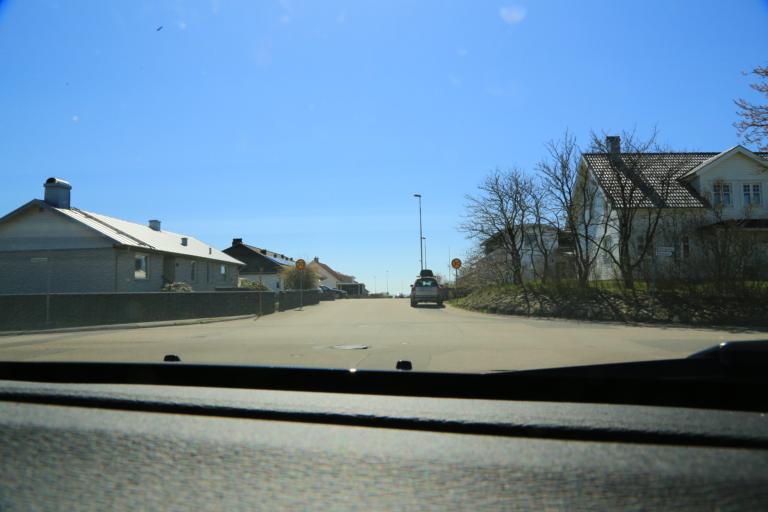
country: SE
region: Halland
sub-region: Varbergs Kommun
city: Traslovslage
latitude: 57.0529
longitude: 12.2827
